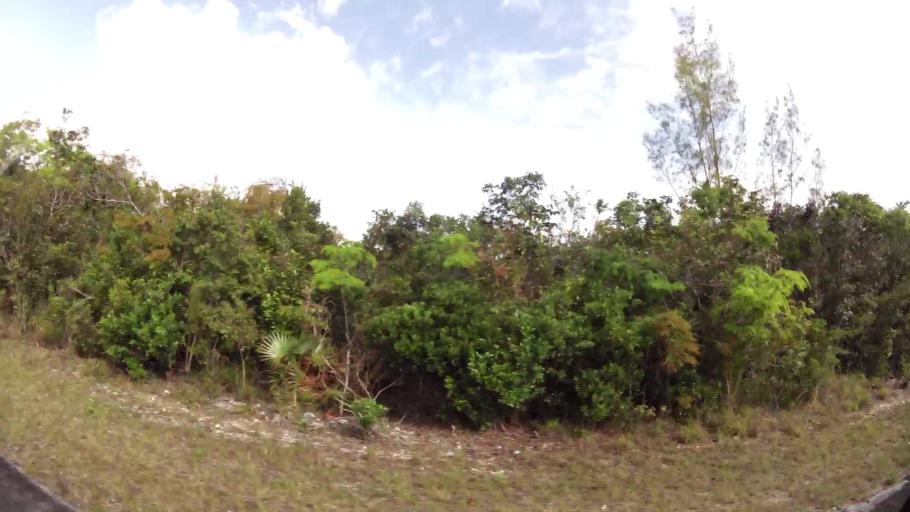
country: BS
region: Freeport
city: Lucaya
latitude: 26.5520
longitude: -78.5506
